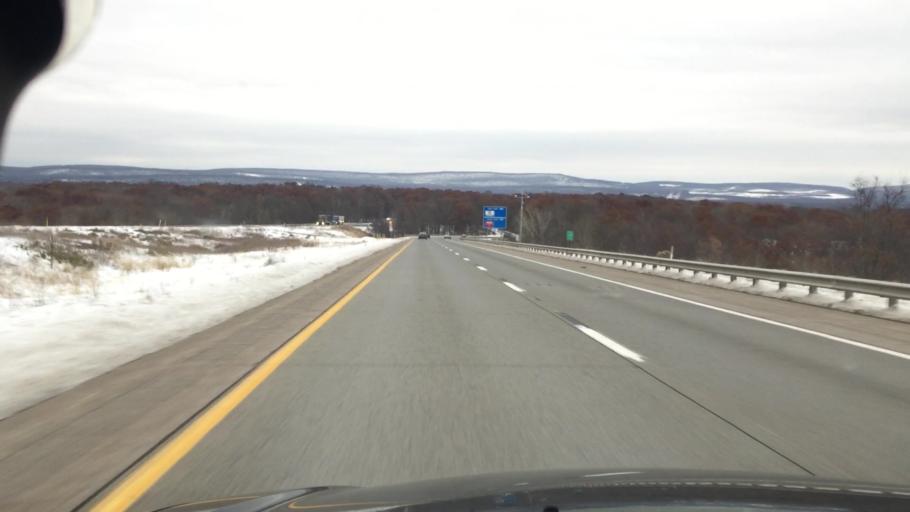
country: US
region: Pennsylvania
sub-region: Luzerne County
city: Nanticoke
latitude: 41.1658
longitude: -75.9564
